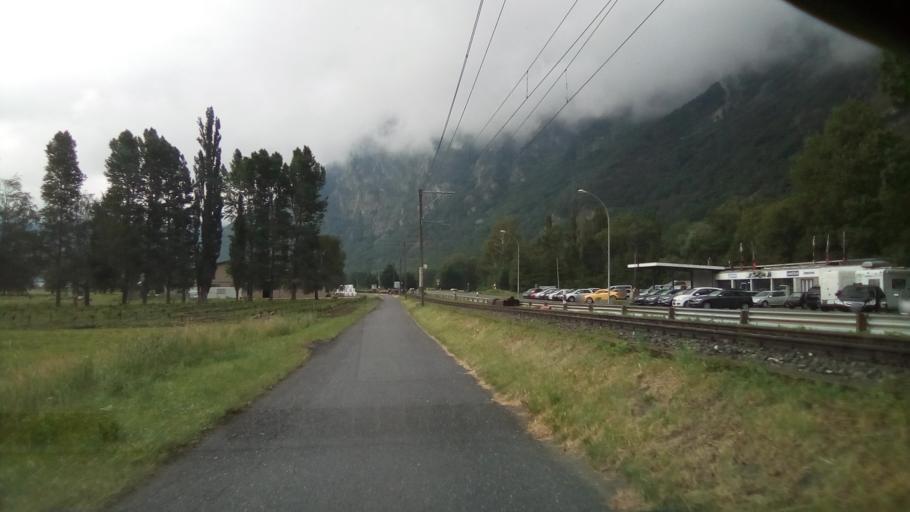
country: CH
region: Valais
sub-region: Saint-Maurice District
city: Vernayaz
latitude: 46.1287
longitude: 7.0457
